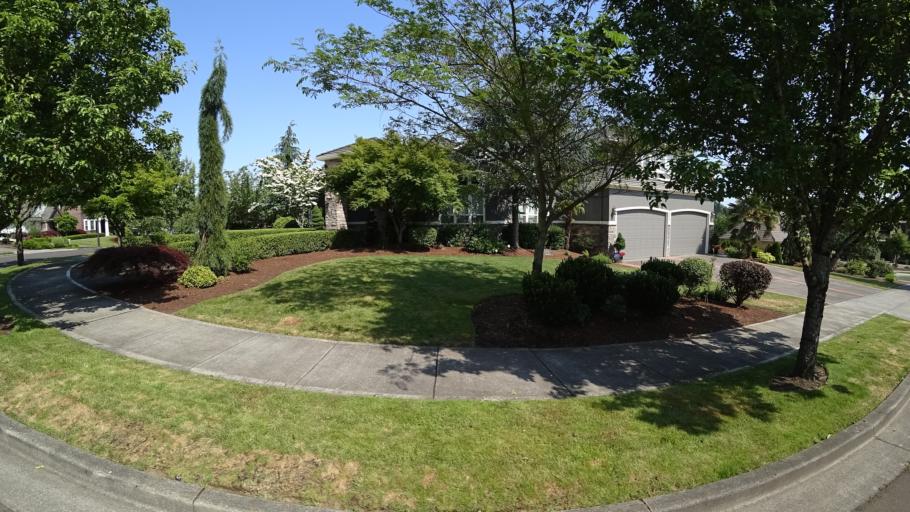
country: US
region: Oregon
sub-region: Clackamas County
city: Happy Valley
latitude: 45.4463
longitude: -122.5349
